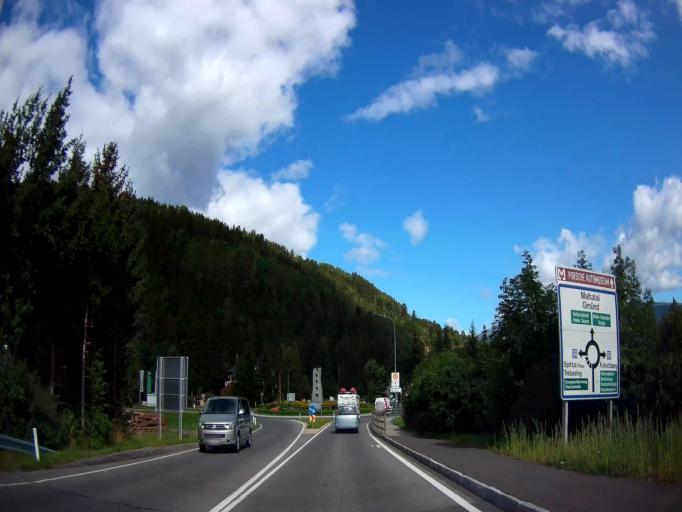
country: AT
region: Carinthia
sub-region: Politischer Bezirk Spittal an der Drau
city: Gmuend
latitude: 46.9031
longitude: 13.5320
